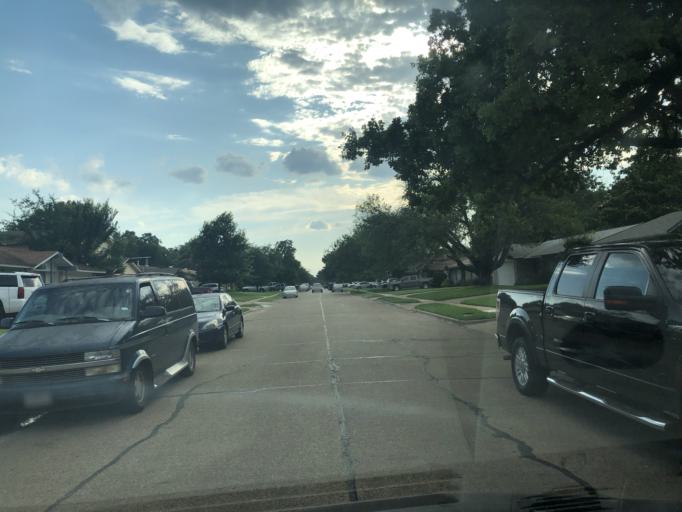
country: US
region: Texas
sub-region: Dallas County
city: Irving
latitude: 32.7891
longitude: -96.9706
